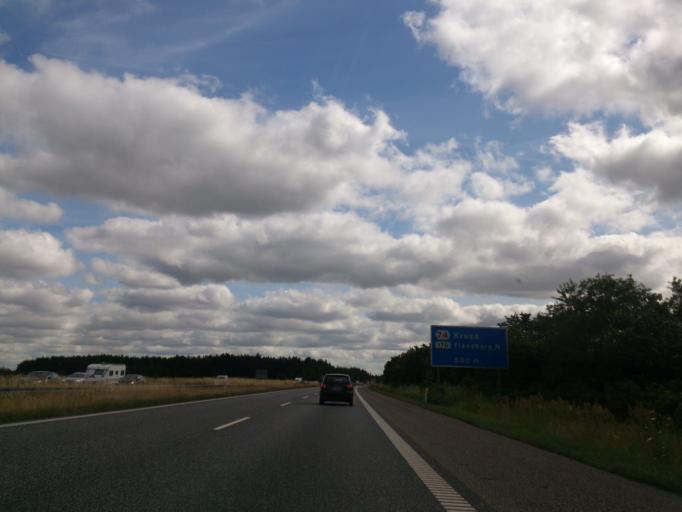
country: DK
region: South Denmark
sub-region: Aabenraa Kommune
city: Krusa
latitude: 54.8864
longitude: 9.3783
